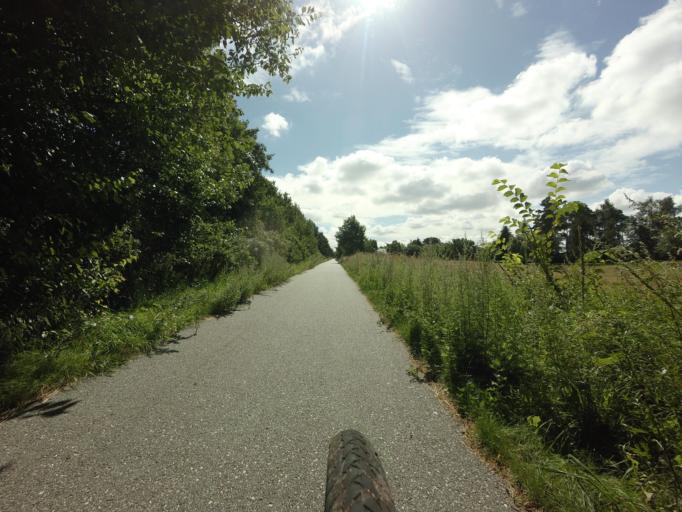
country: DK
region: Central Jutland
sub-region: Norddjurs Kommune
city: Auning
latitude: 56.4358
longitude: 10.3723
